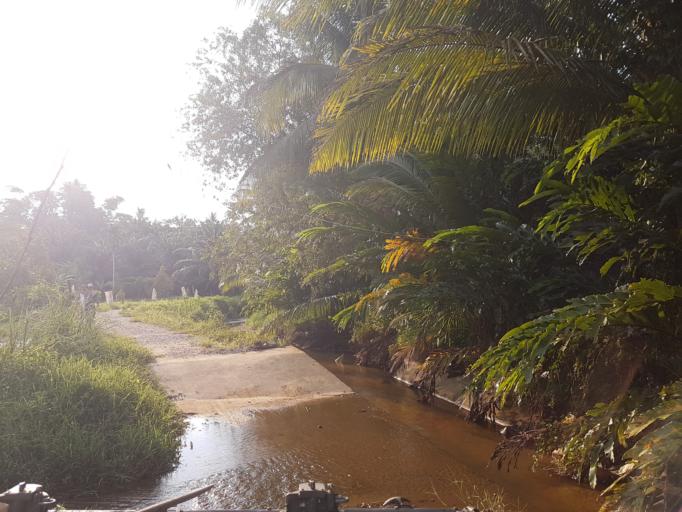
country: TH
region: Pattani
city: Khok Pho
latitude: 6.6657
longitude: 101.0879
